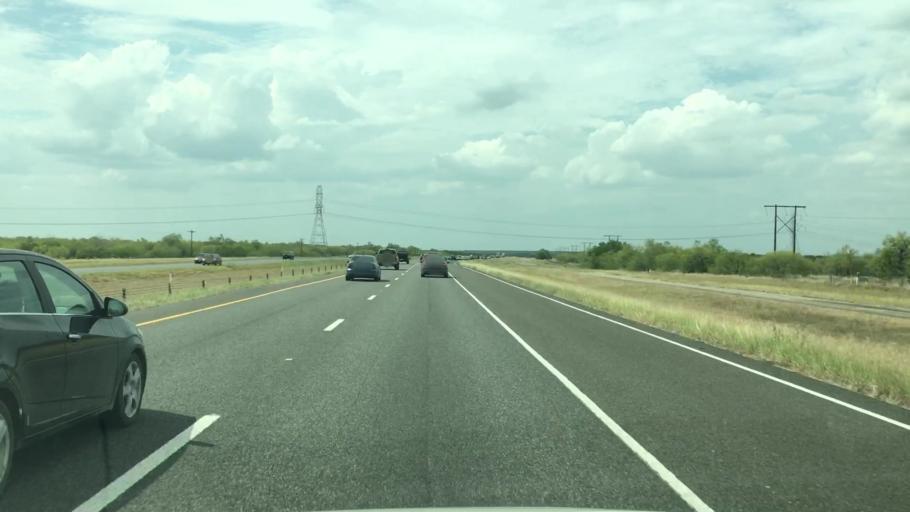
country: US
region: Texas
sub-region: Atascosa County
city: Pleasanton
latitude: 28.8181
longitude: -98.3589
